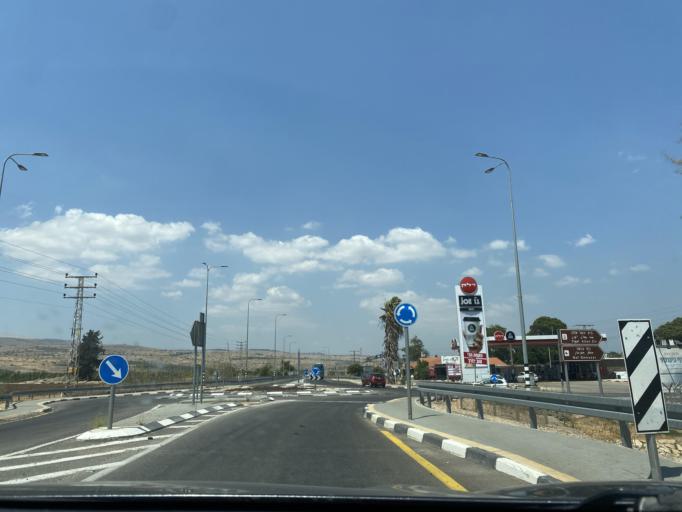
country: IL
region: Northern District
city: Tiberias
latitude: 32.8444
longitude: 35.5156
